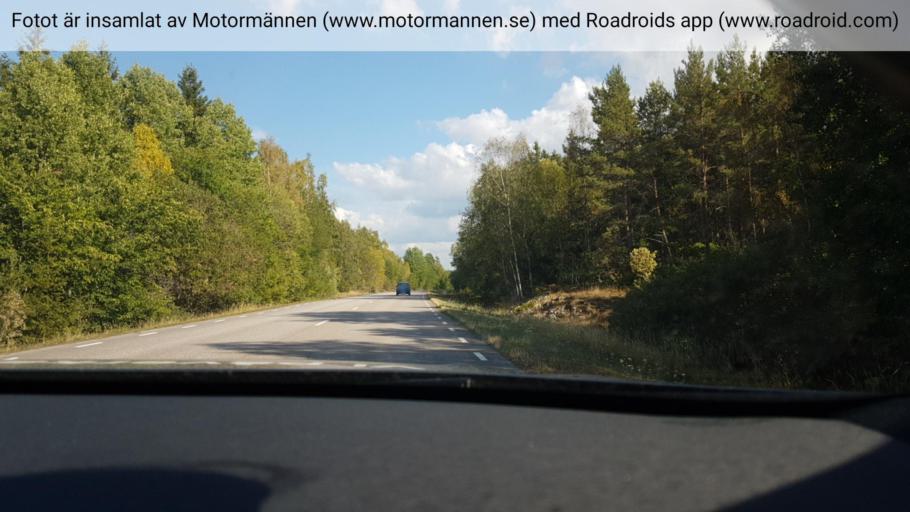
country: SE
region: Vaestra Goetaland
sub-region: Gotene Kommun
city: Goetene
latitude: 58.6226
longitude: 13.4760
